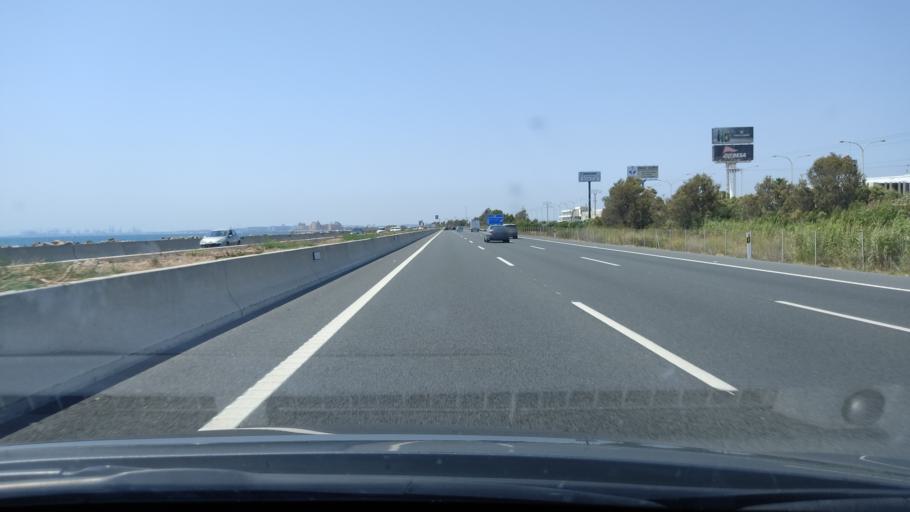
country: ES
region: Valencia
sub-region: Provincia de Valencia
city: Albuixech
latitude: 39.5388
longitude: -0.3057
